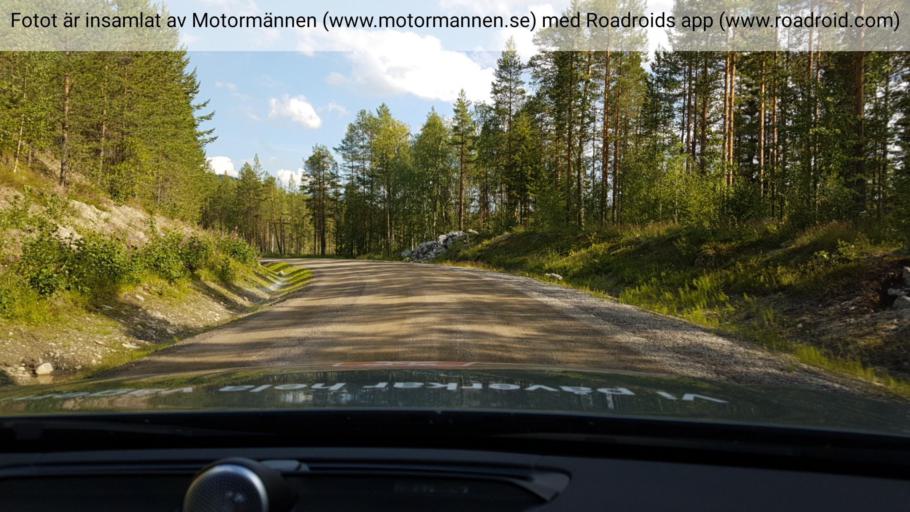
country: SE
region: Vaesterbotten
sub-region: Dorotea Kommun
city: Dorotea
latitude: 63.9731
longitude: 16.0586
